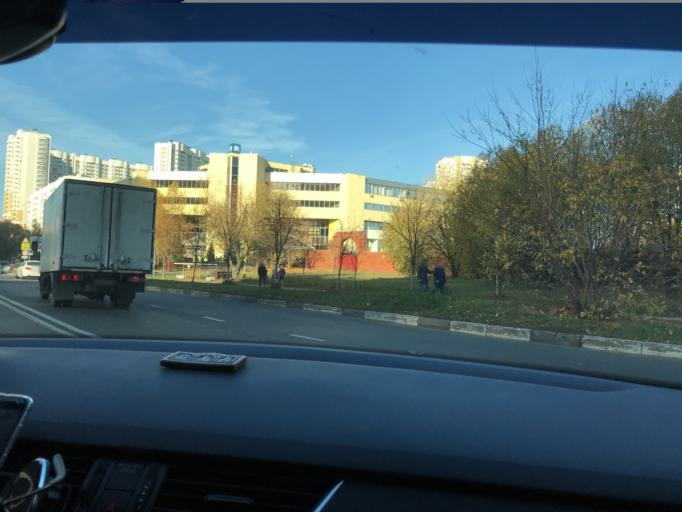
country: RU
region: Moscow
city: Khimki
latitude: 55.8828
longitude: 37.4289
